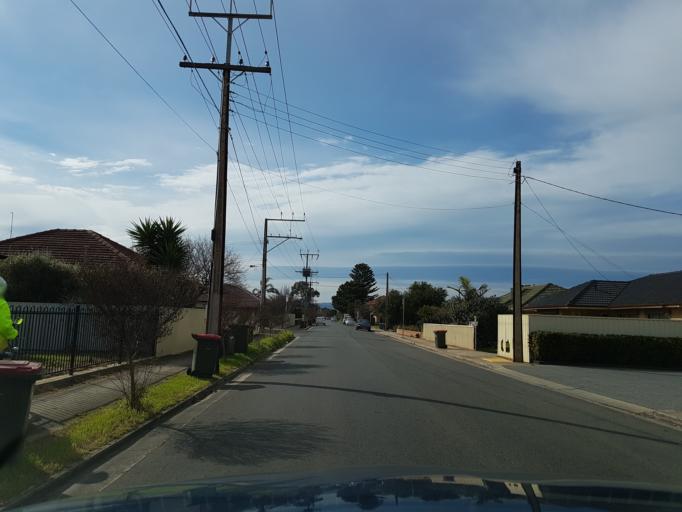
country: AU
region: South Australia
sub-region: City of West Torrens
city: Plympton
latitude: -34.9308
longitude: 138.5388
